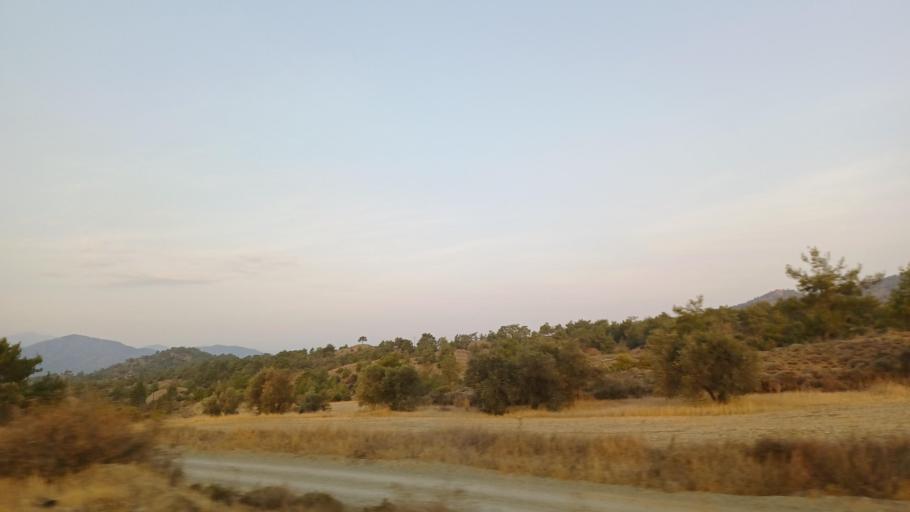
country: CY
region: Larnaka
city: Kornos
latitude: 34.9176
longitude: 33.3833
